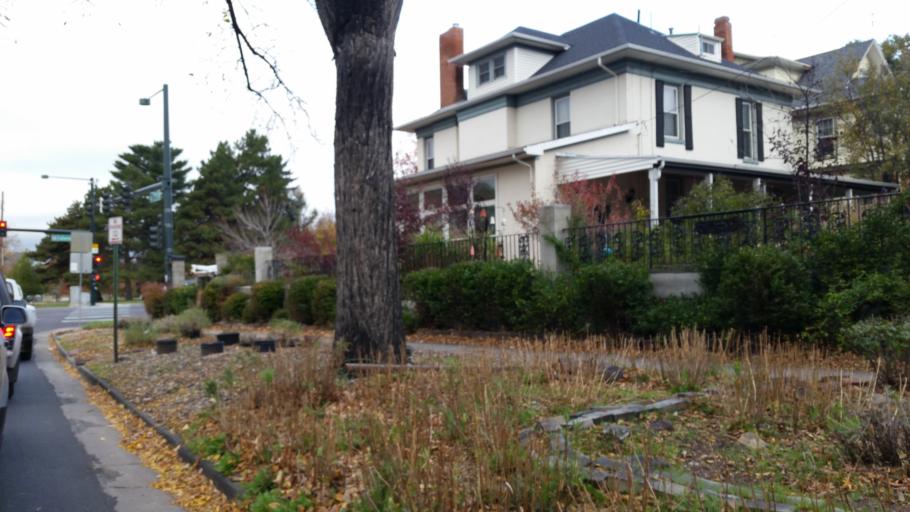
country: US
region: Colorado
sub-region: Arapahoe County
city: Glendale
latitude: 39.7438
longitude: -104.9402
